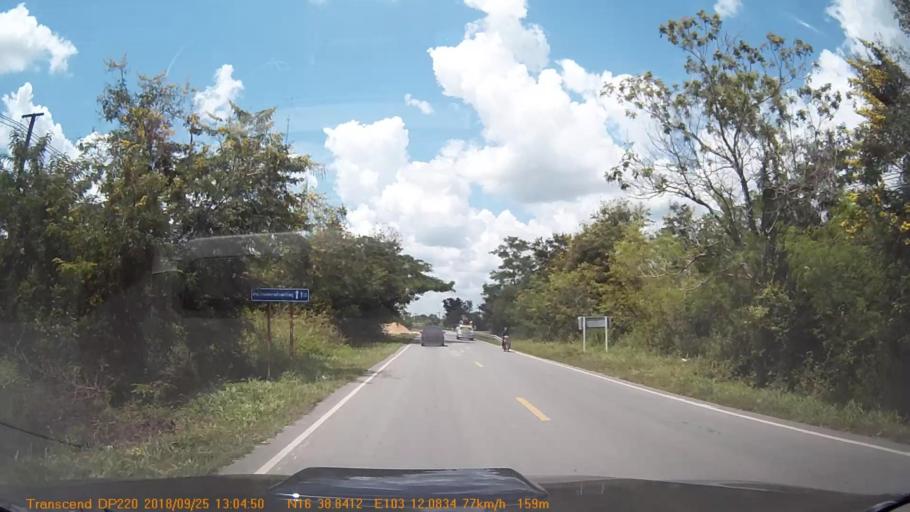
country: TH
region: Kalasin
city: Huai Mek
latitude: 16.6475
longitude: 103.2013
